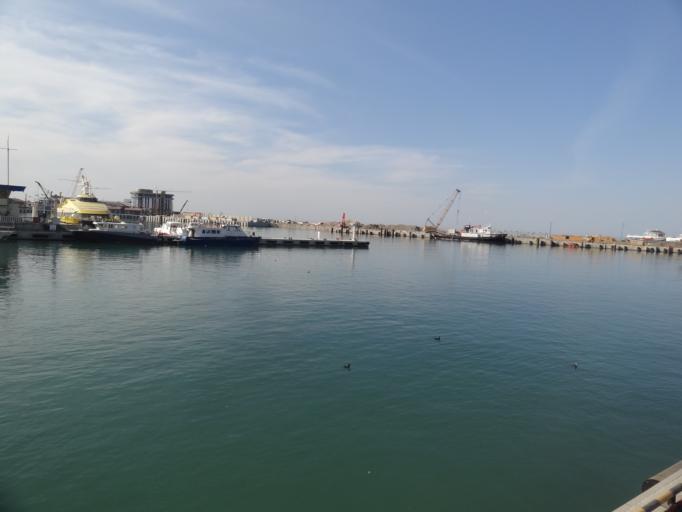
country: RU
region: Krasnodarskiy
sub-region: Sochi City
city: Sochi
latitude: 43.5822
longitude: 39.7184
